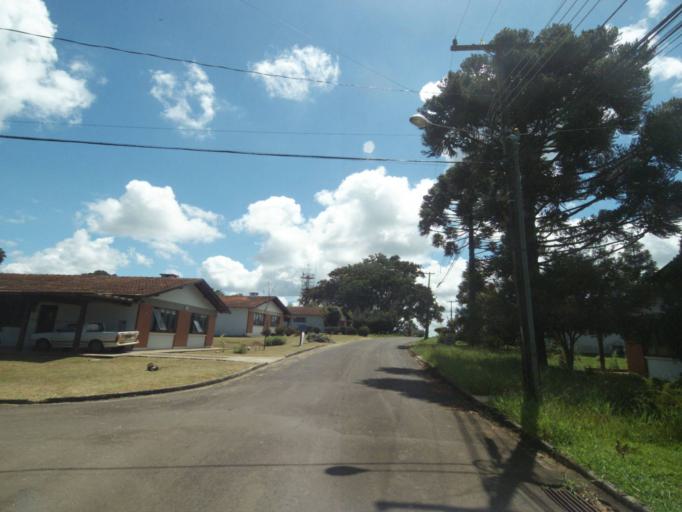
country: BR
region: Parana
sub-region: Chopinzinho
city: Chopinzinho
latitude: -25.7944
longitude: -52.0895
